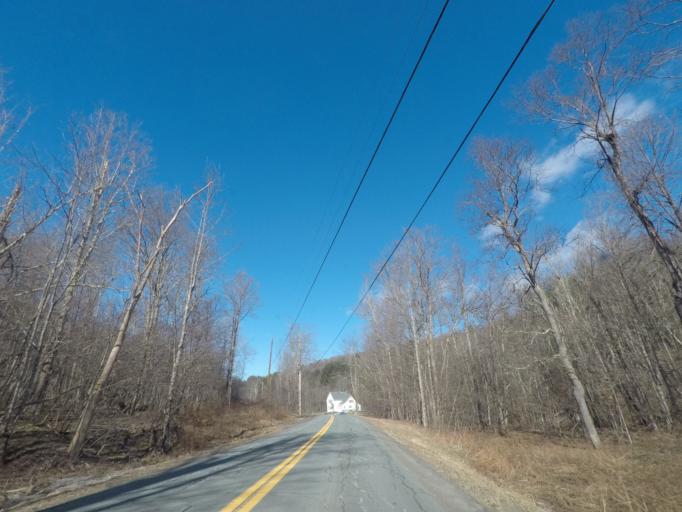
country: US
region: Massachusetts
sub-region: Berkshire County
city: Williamstown
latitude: 42.7415
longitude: -73.3376
